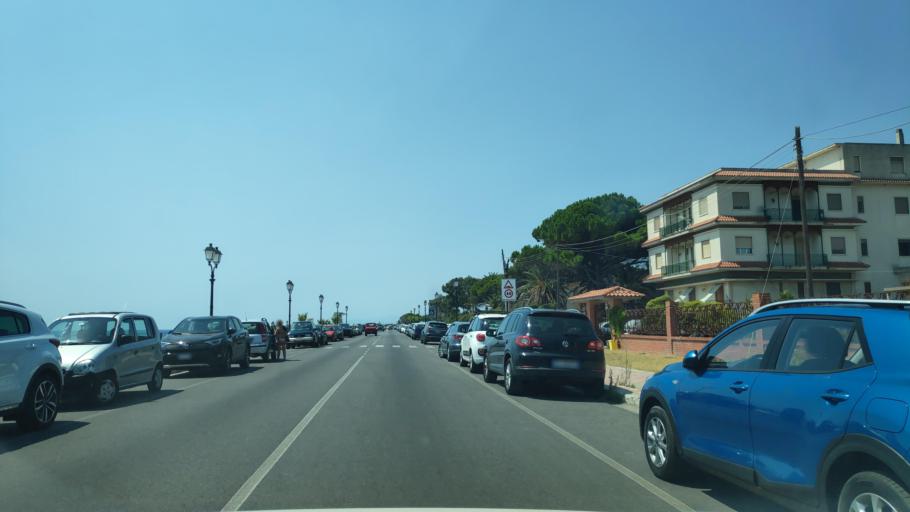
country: IT
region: Calabria
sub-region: Provincia di Reggio Calabria
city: Siderno
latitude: 38.2719
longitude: 16.3038
